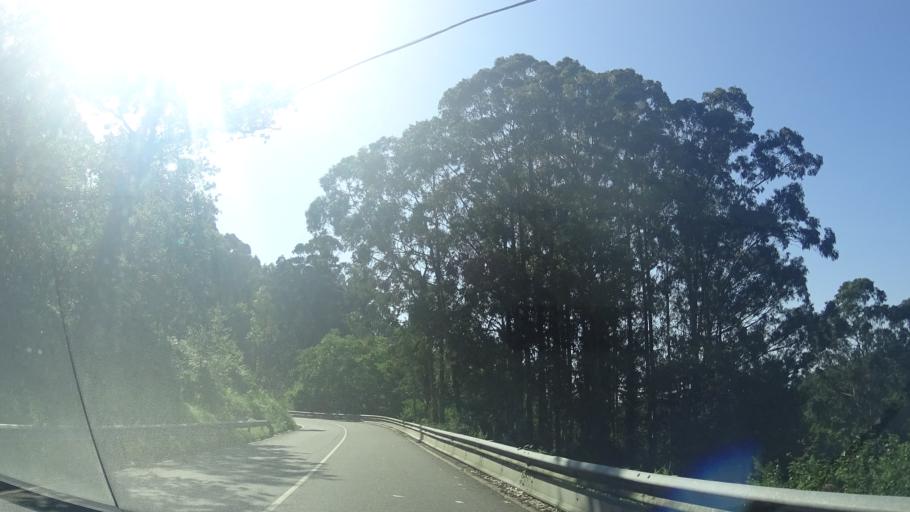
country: ES
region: Asturias
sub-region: Province of Asturias
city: Ribadesella
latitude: 43.4639
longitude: -5.0942
